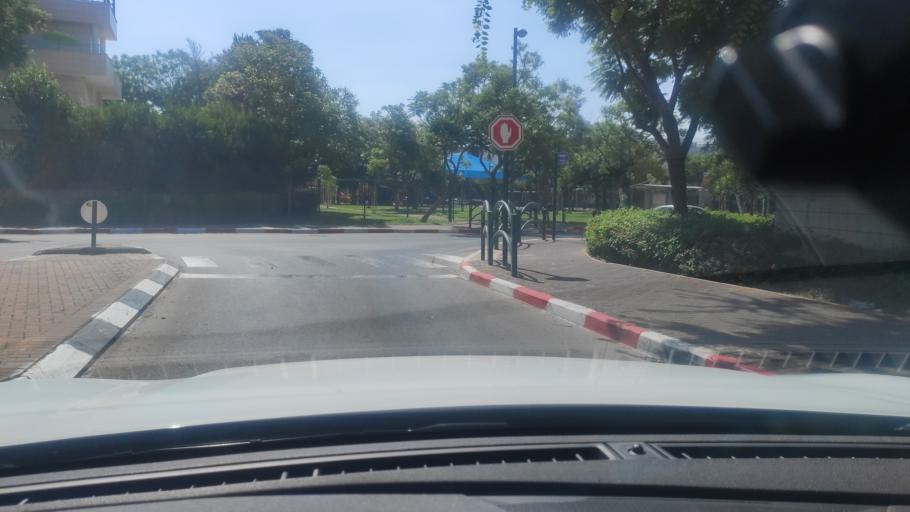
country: IL
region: Central District
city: Kfar Saba
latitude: 32.1787
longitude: 34.9348
